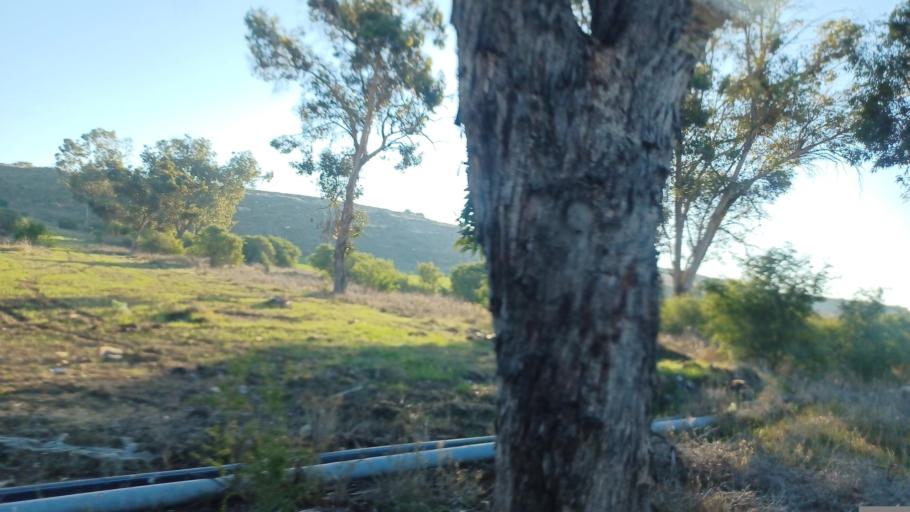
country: CY
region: Lefkosia
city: Mammari
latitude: 35.1563
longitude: 33.2626
